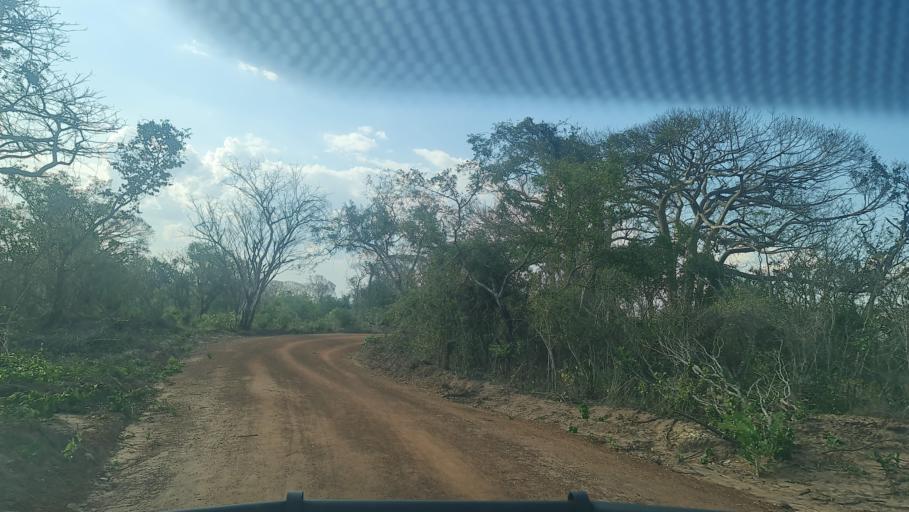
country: MZ
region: Nampula
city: Ilha de Mocambique
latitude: -15.5098
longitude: 40.1638
